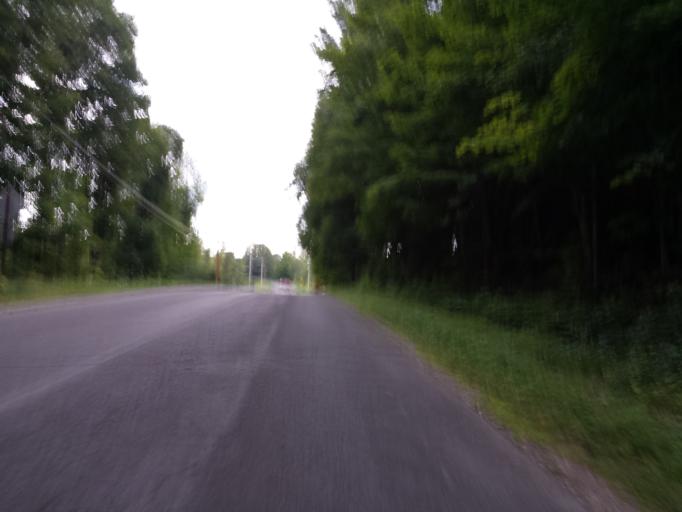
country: US
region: New York
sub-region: St. Lawrence County
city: Potsdam
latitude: 44.6871
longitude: -75.0126
